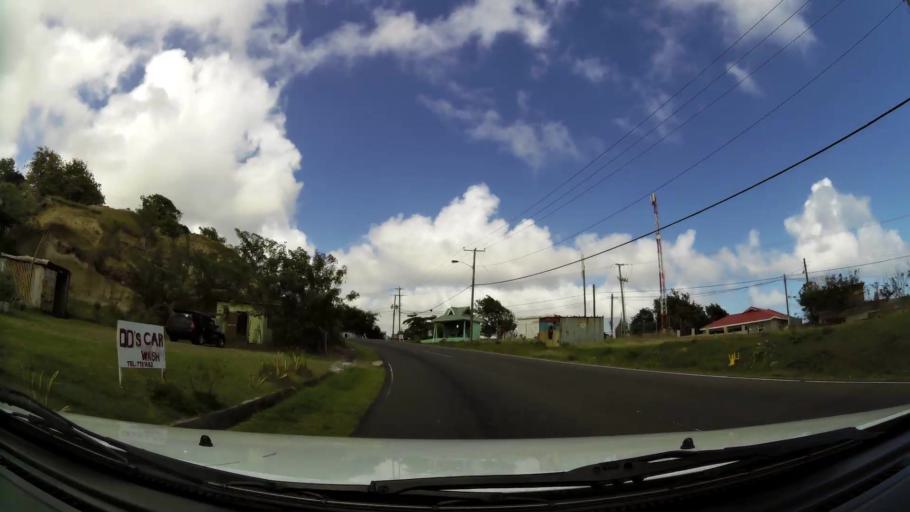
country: LC
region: Dennery Quarter
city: Dennery
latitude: 13.9169
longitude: -60.8923
